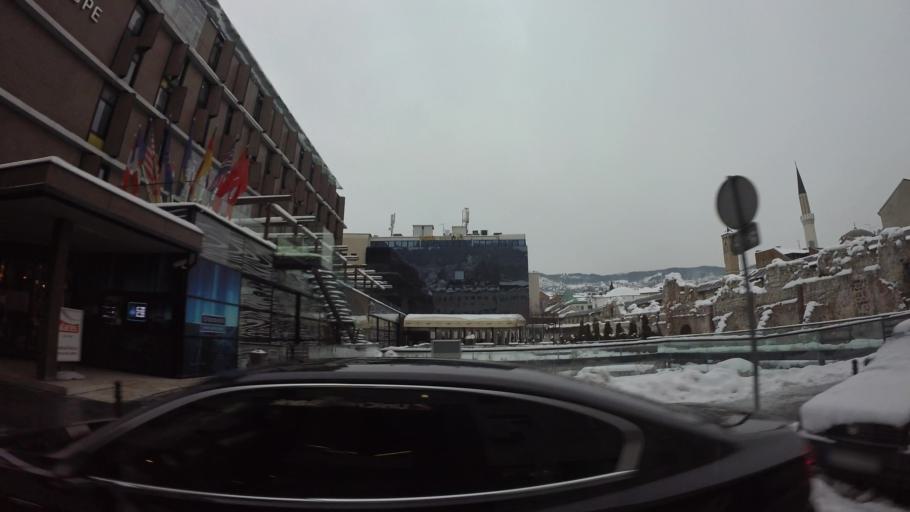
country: BA
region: Federation of Bosnia and Herzegovina
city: Kobilja Glava
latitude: 43.8583
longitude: 18.4277
